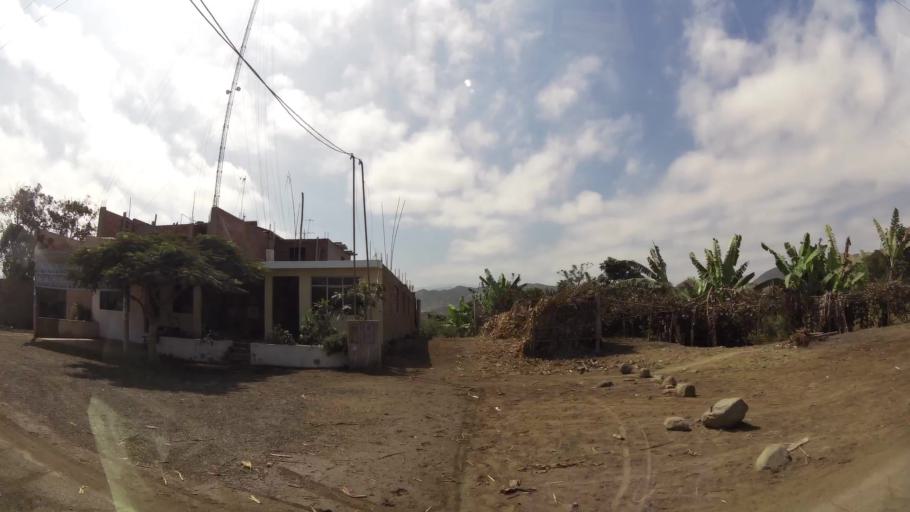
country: PE
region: Lima
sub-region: Provincia de Canete
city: Mala
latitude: -12.7186
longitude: -76.6185
